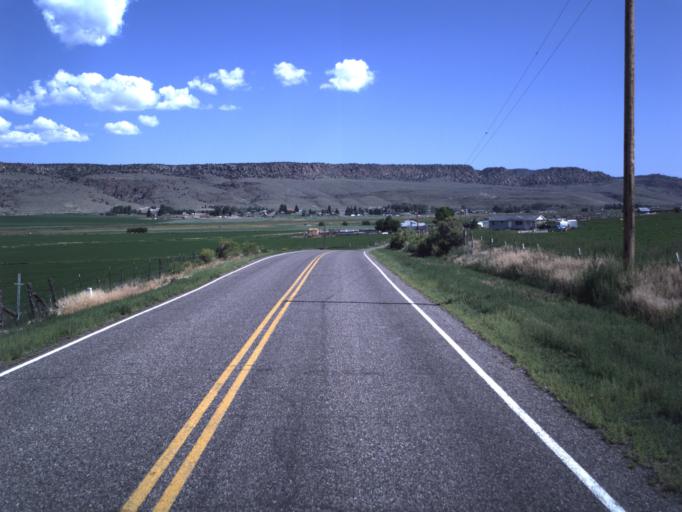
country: US
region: Utah
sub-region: Wayne County
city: Loa
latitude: 38.4342
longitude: -111.6202
